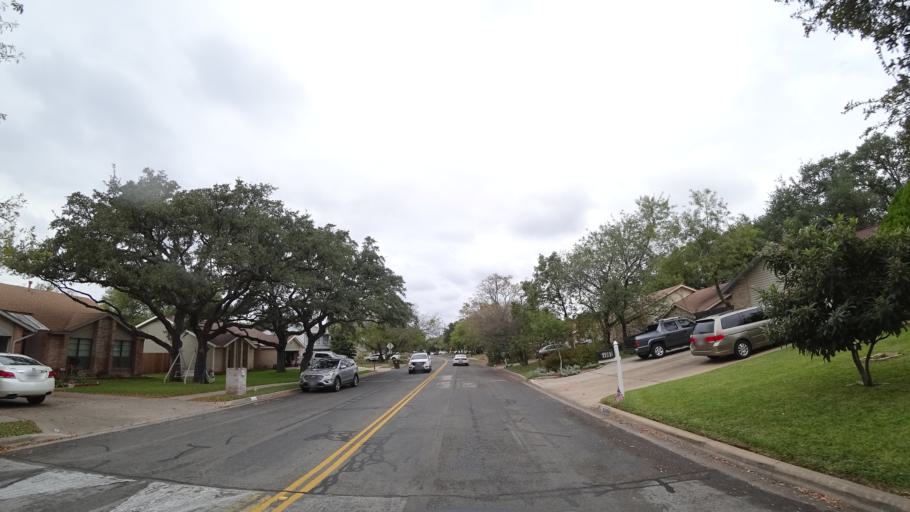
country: US
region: Texas
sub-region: Williamson County
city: Round Rock
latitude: 30.4921
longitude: -97.6993
